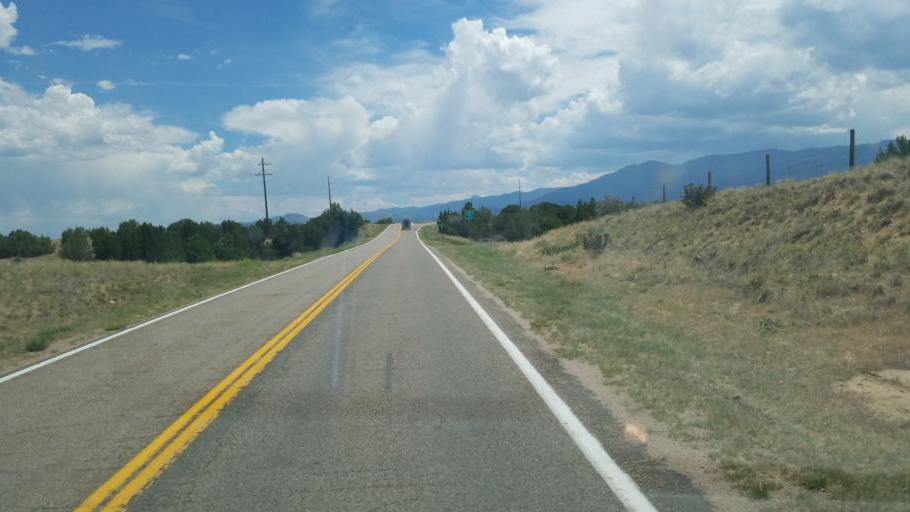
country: US
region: Colorado
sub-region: Fremont County
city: Florence
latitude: 38.3297
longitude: -105.1056
